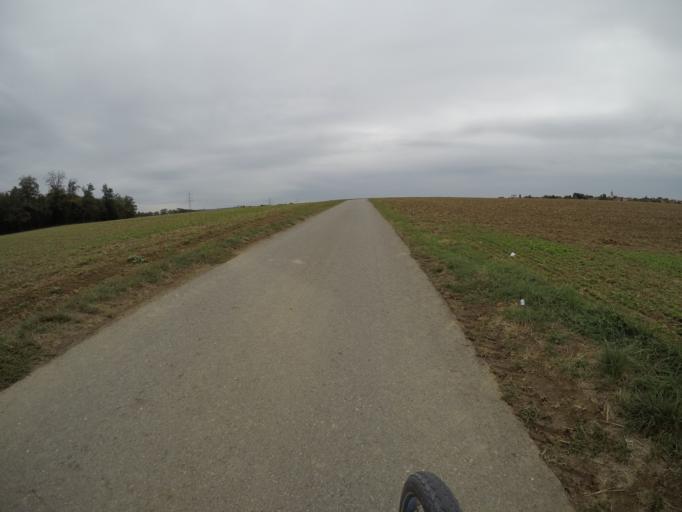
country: DE
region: Baden-Wuerttemberg
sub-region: Regierungsbezirk Stuttgart
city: Eberdingen
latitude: 48.8607
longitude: 8.9899
